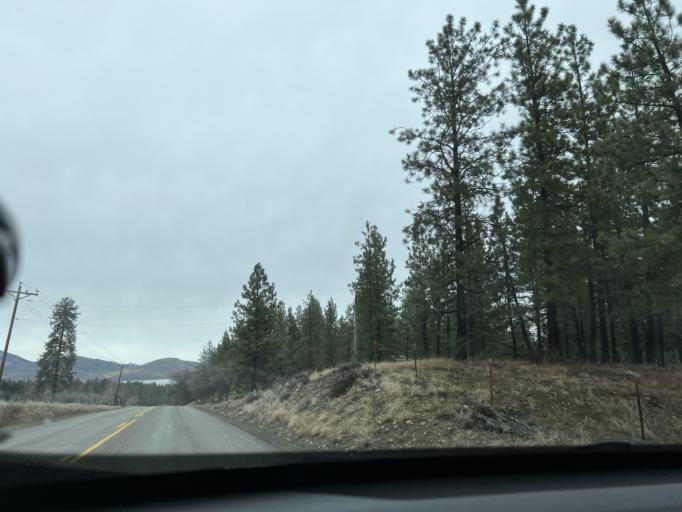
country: US
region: Washington
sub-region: Okanogan County
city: Brewster
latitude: 48.4567
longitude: -120.2057
